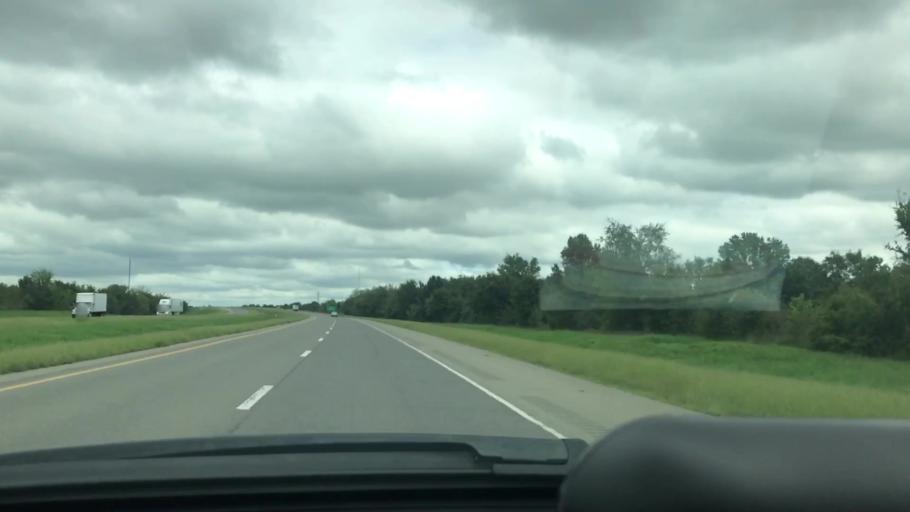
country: US
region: Oklahoma
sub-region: McIntosh County
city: Checotah
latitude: 35.5651
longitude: -95.4921
